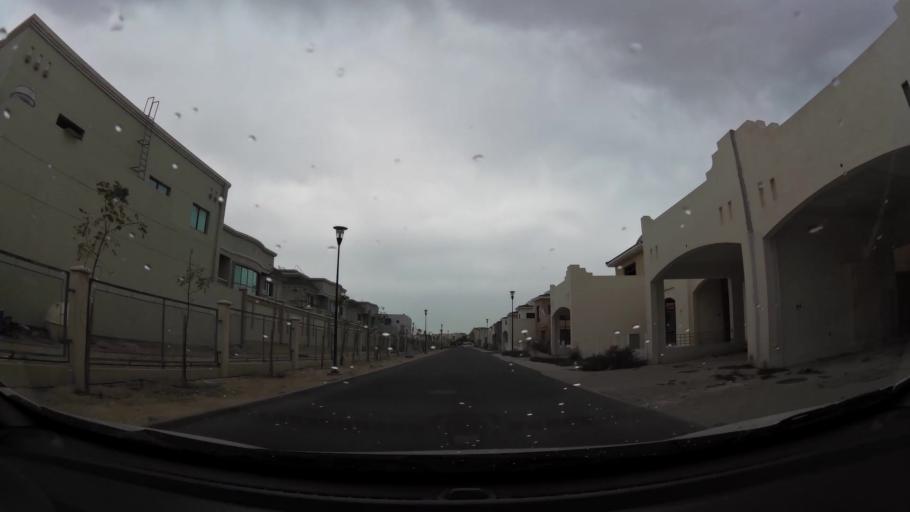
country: BH
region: Northern
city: Ar Rifa'
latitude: 26.0907
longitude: 50.5592
